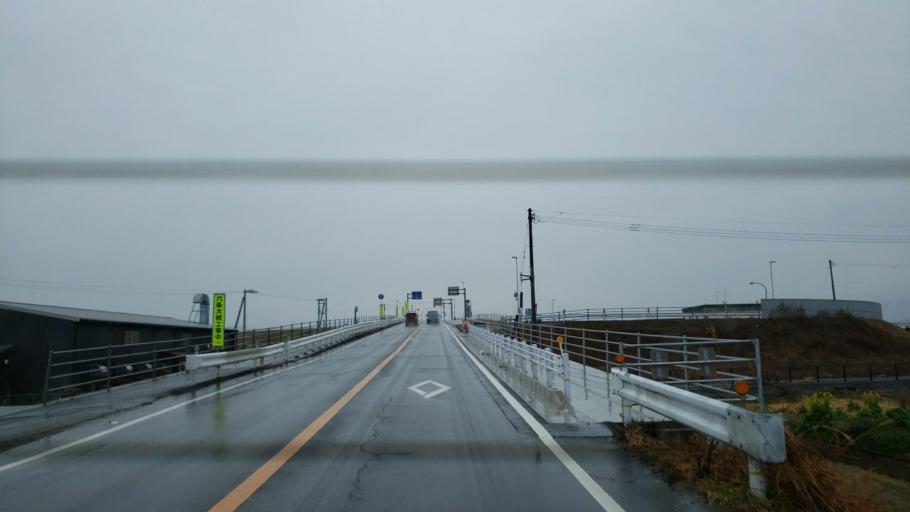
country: JP
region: Tokushima
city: Ishii
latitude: 34.1100
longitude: 134.4367
